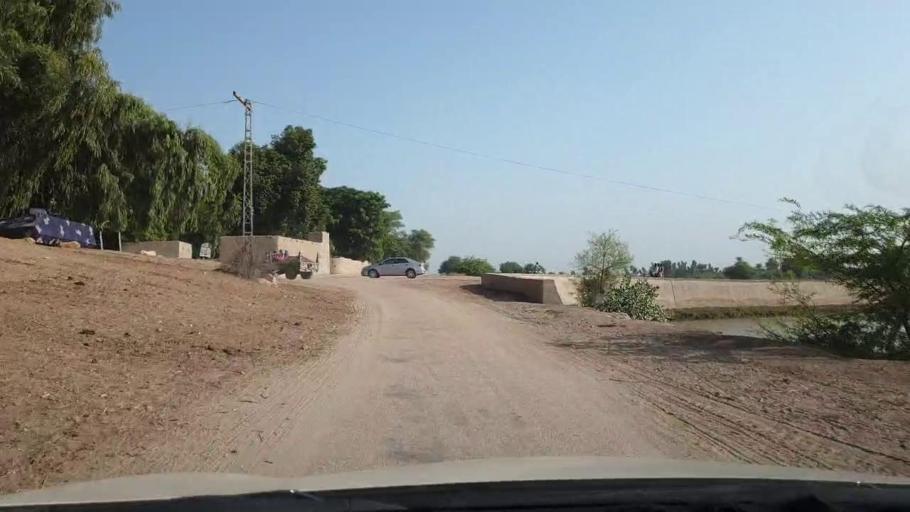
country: PK
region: Sindh
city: Larkana
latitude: 27.5505
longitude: 68.2562
